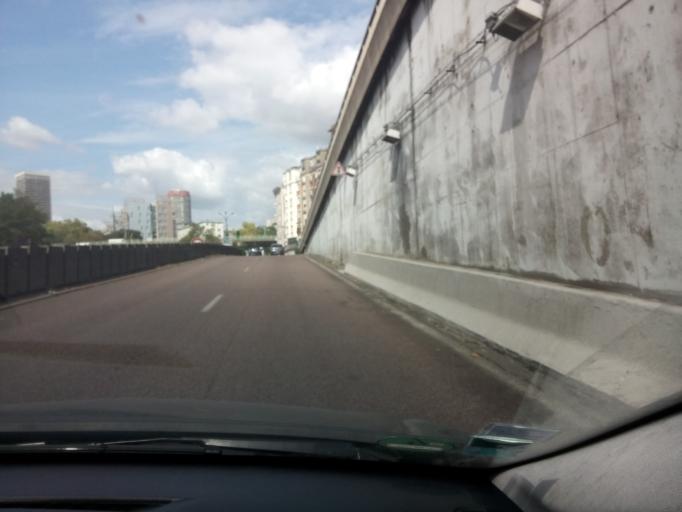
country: FR
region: Ile-de-France
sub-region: Departement du Val-de-Marne
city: Gentilly
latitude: 48.8036
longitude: 2.3434
